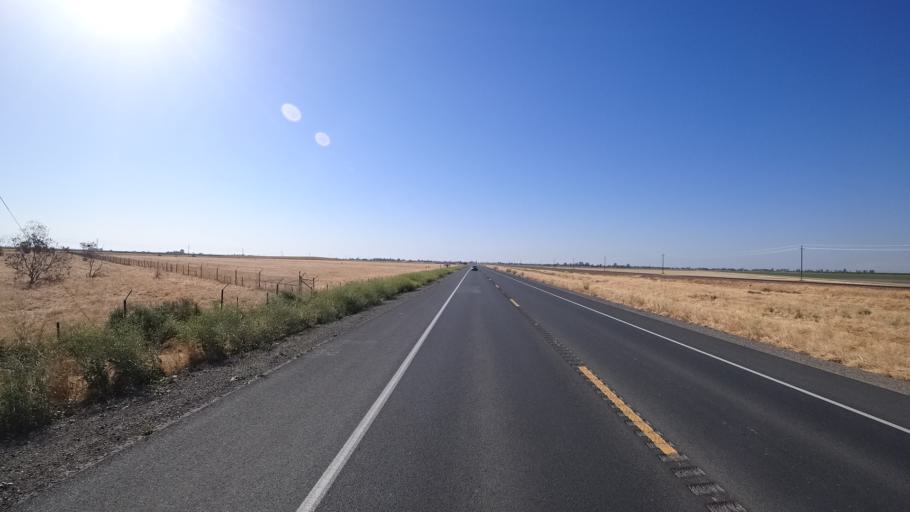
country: US
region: California
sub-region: Kings County
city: Corcoran
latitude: 36.1365
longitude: -119.5840
